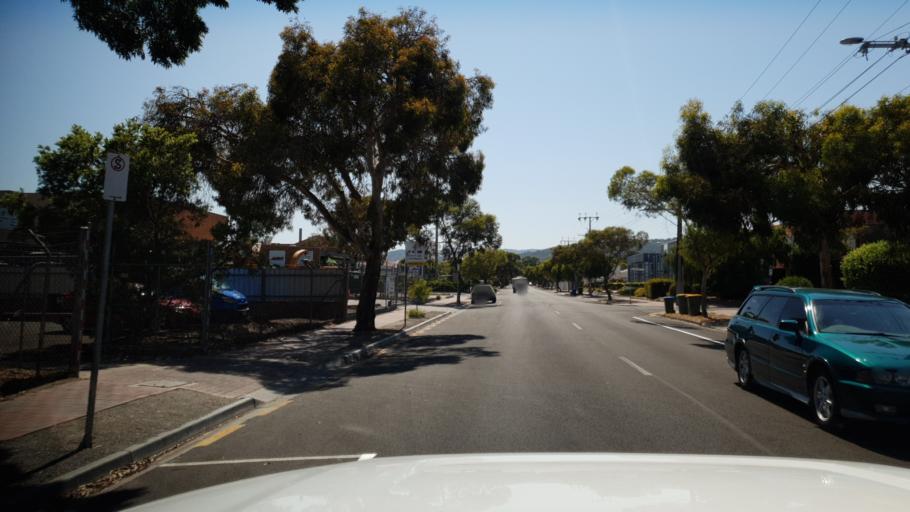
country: AU
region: South Australia
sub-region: Marion
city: Clovelly Park
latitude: -34.9908
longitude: 138.5781
